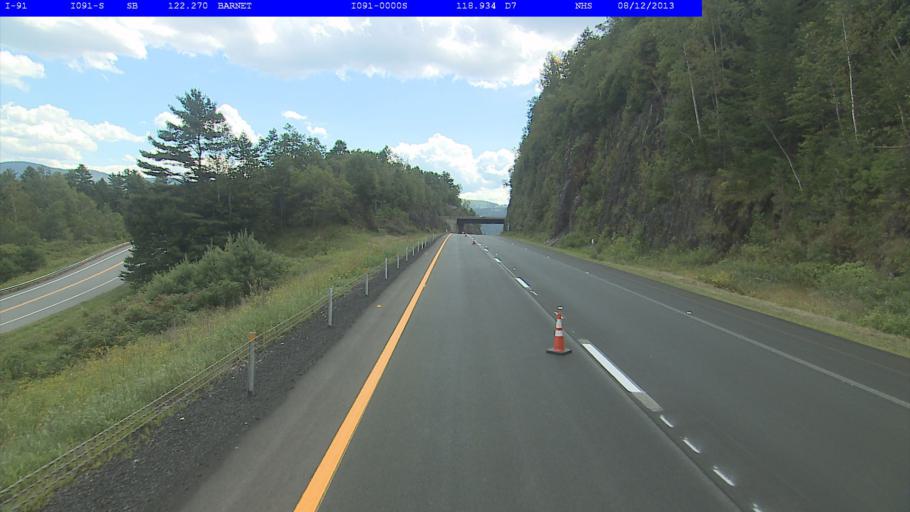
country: US
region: Vermont
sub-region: Caledonia County
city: Saint Johnsbury
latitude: 44.3145
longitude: -72.0370
